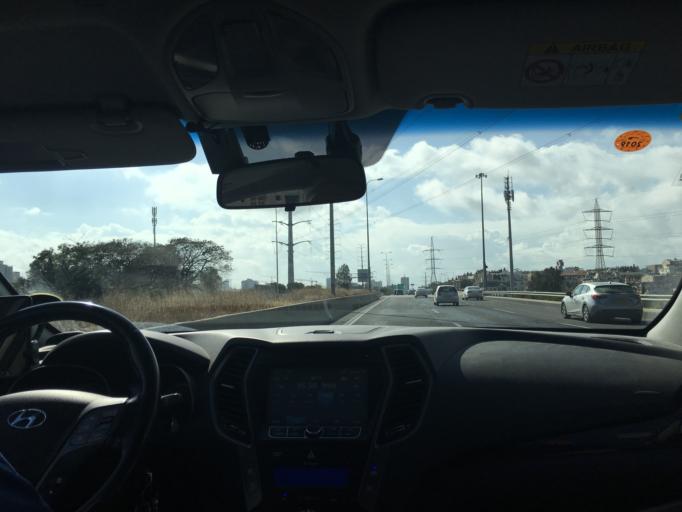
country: IL
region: Tel Aviv
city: Giv`at Shemu'el
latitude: 32.0937
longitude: 34.8458
